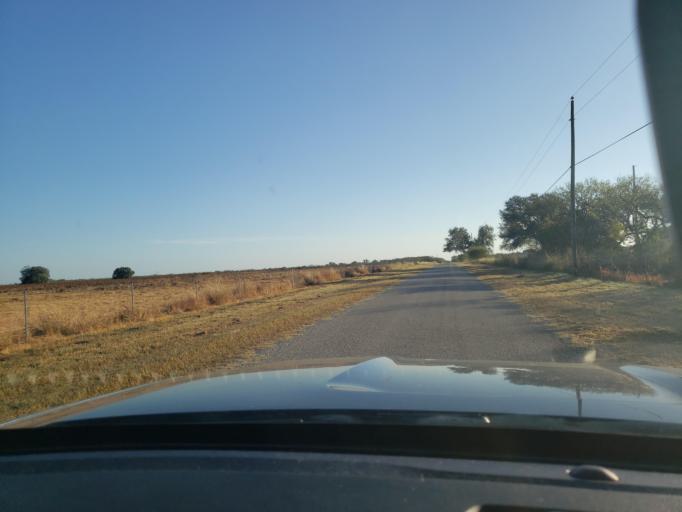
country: US
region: Texas
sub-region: Bee County
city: Beeville
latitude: 28.4302
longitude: -97.6912
